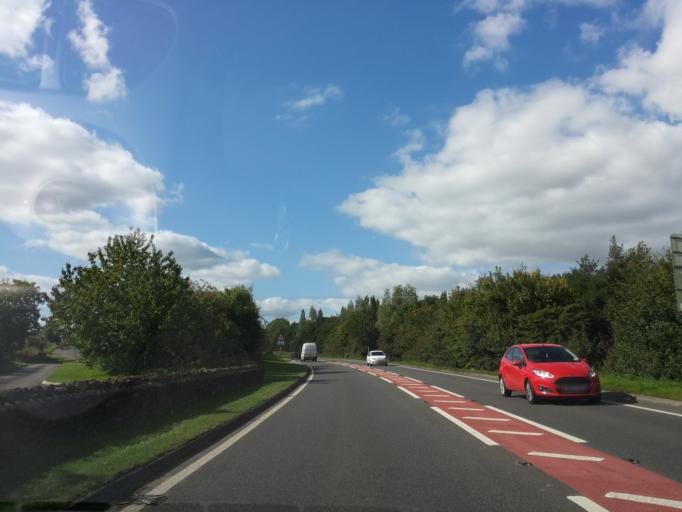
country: GB
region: England
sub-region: Wiltshire
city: Chapmanslade
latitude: 51.2553
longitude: -2.2620
